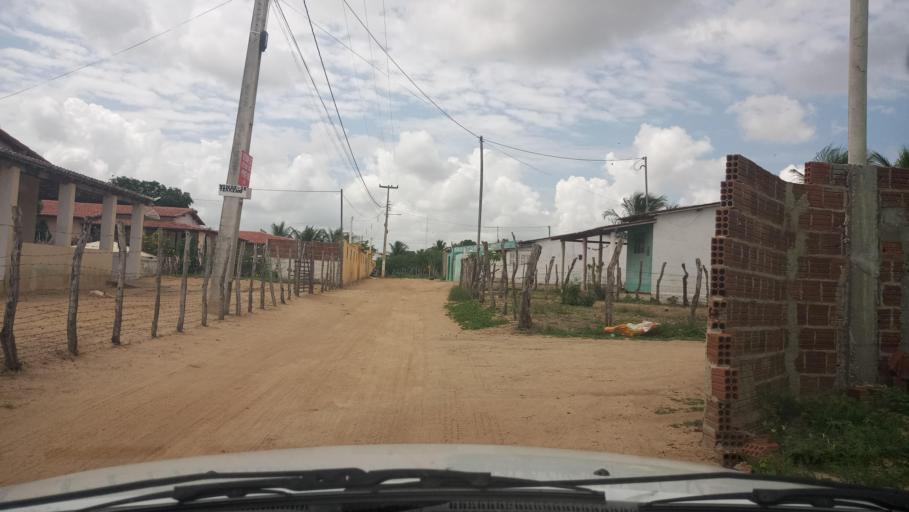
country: BR
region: Rio Grande do Norte
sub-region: Sao Paulo Do Potengi
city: Sao Paulo do Potengi
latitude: -5.9125
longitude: -35.6952
